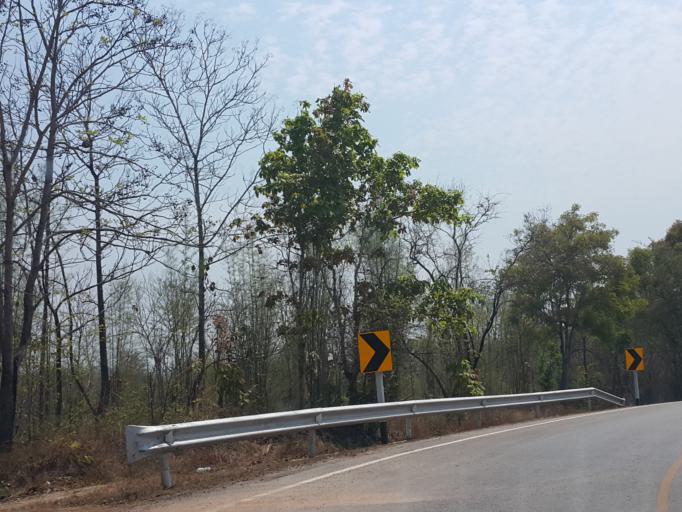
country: TH
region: Lampang
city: Mueang Pan
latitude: 18.7688
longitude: 99.5552
